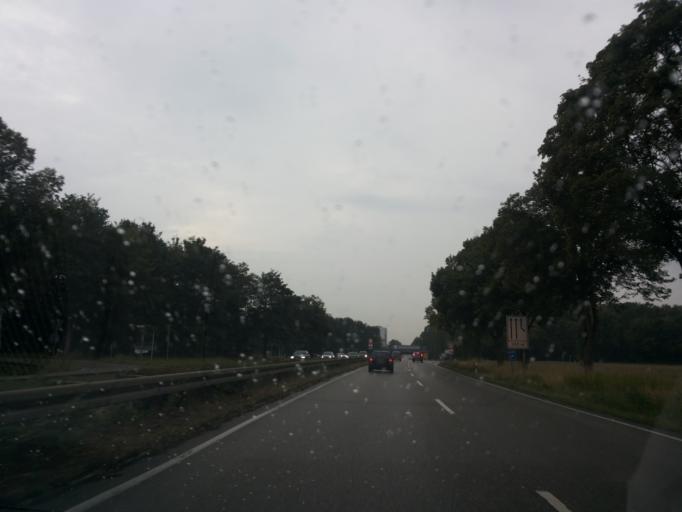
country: DE
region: Bavaria
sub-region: Upper Bavaria
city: Lenting
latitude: 48.7725
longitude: 11.4654
